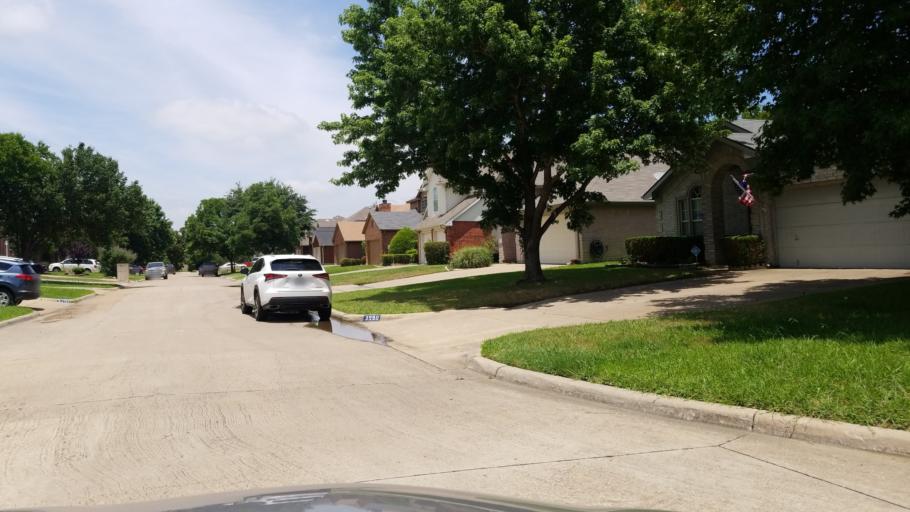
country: US
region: Texas
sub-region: Dallas County
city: Grand Prairie
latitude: 32.6775
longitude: -96.9901
